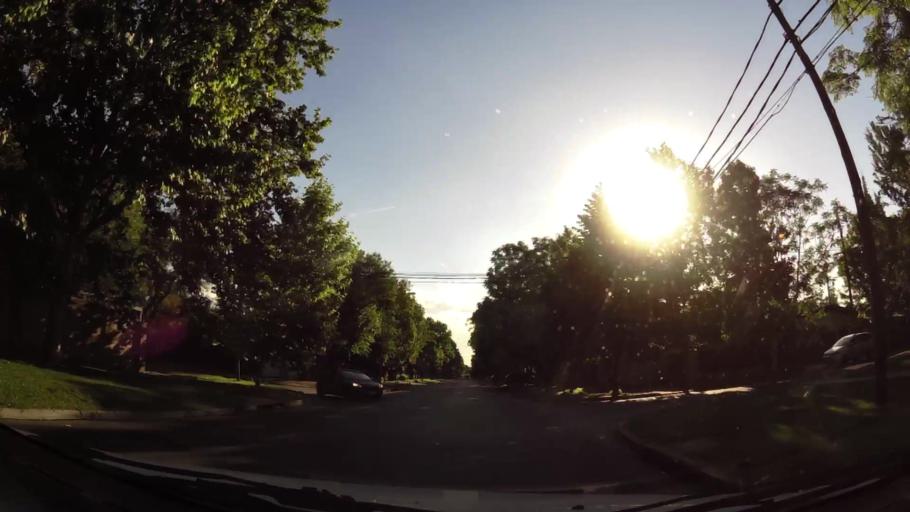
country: AR
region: Buenos Aires
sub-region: Partido de San Isidro
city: San Isidro
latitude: -34.4830
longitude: -58.5404
